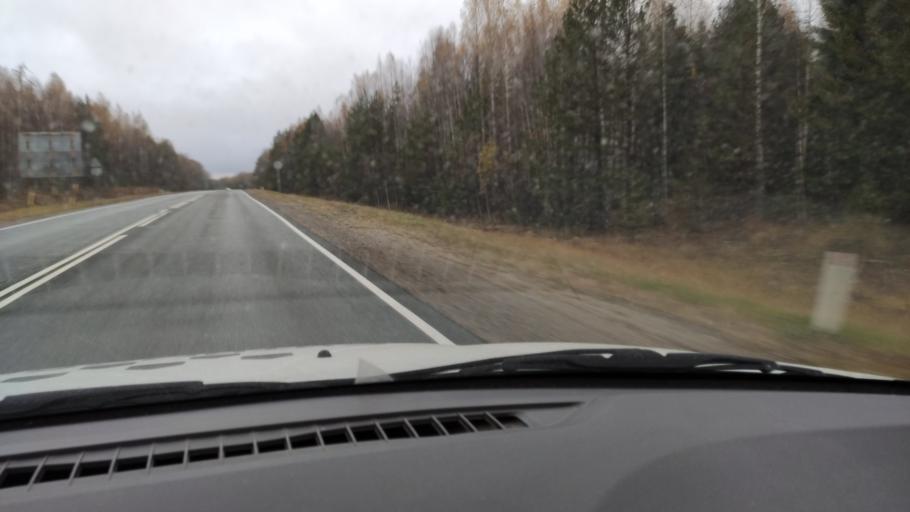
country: RU
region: Kirov
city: Dubrovka
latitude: 58.8949
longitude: 51.3294
